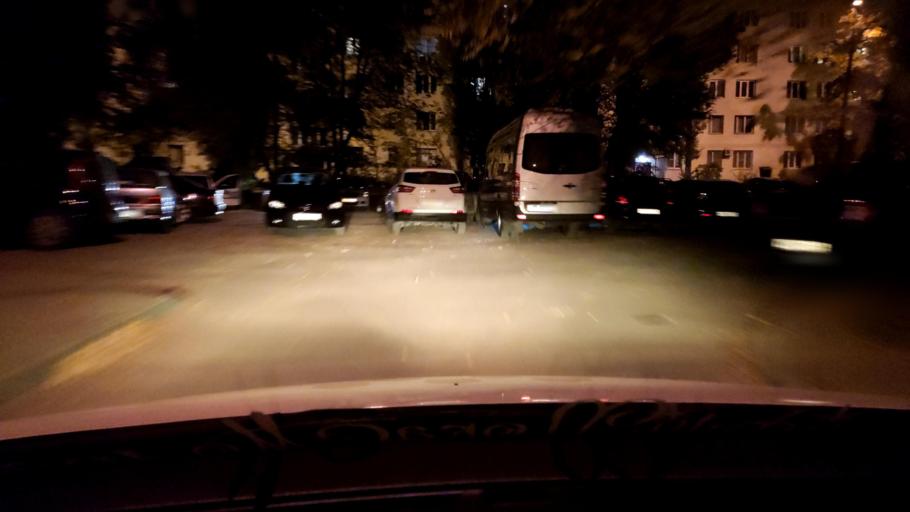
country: RU
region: Voronezj
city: Pridonskoy
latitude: 51.6528
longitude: 39.1198
